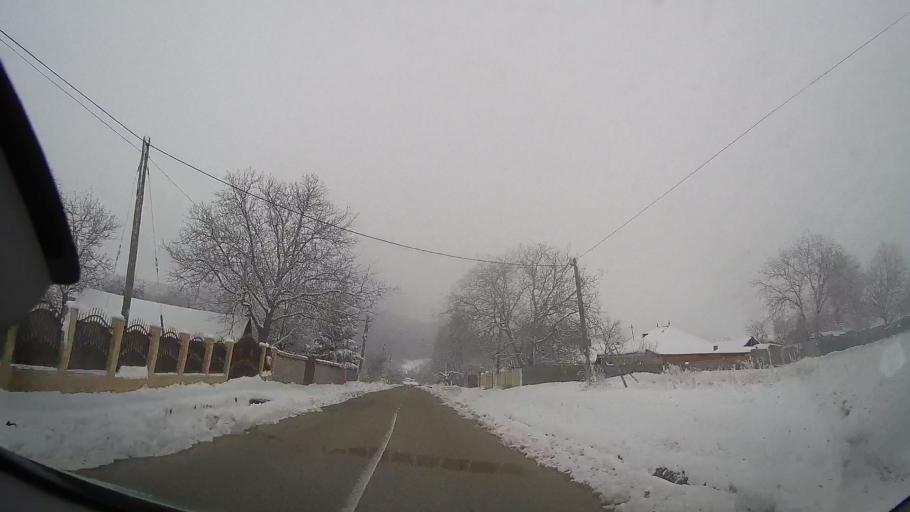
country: RO
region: Neamt
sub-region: Comuna Bozieni
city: Bozieni
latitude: 46.8390
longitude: 27.1669
